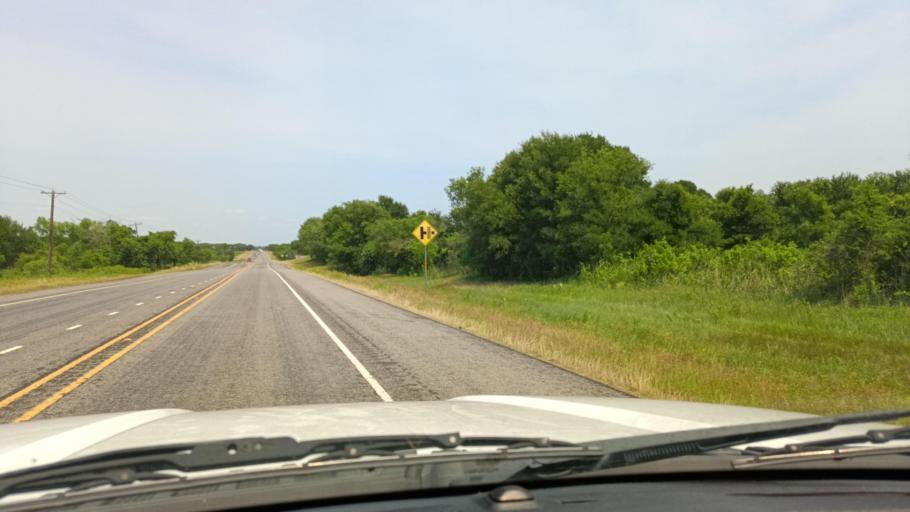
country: US
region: Texas
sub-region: Milam County
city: Cameron
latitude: 30.8489
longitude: -97.0382
